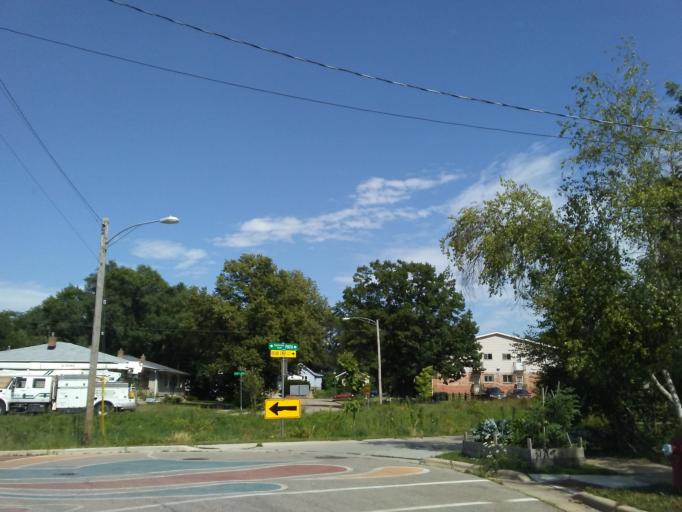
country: US
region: Wisconsin
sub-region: Dane County
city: Monona
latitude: 43.1006
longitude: -89.3392
